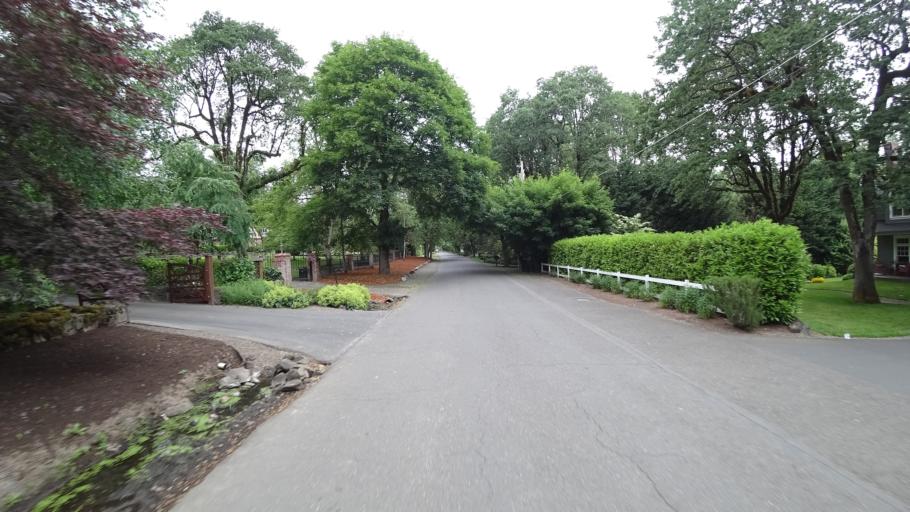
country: US
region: Oregon
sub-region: Clackamas County
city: Lake Oswego
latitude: 45.4340
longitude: -122.6588
